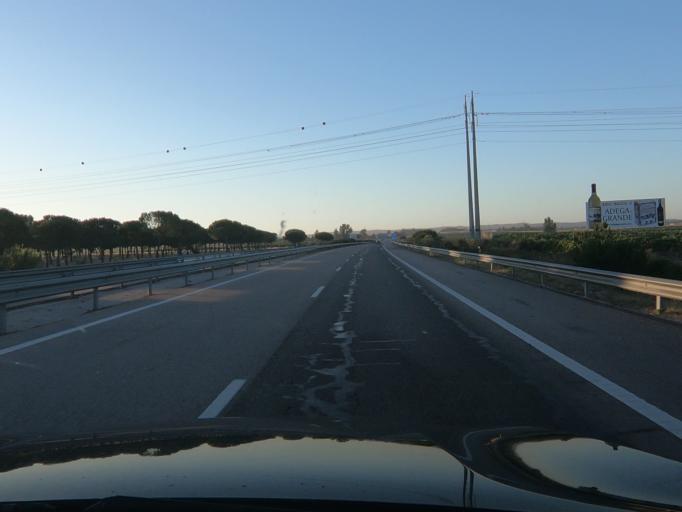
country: PT
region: Santarem
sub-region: Almeirim
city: Almeirim
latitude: 39.1869
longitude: -8.6422
